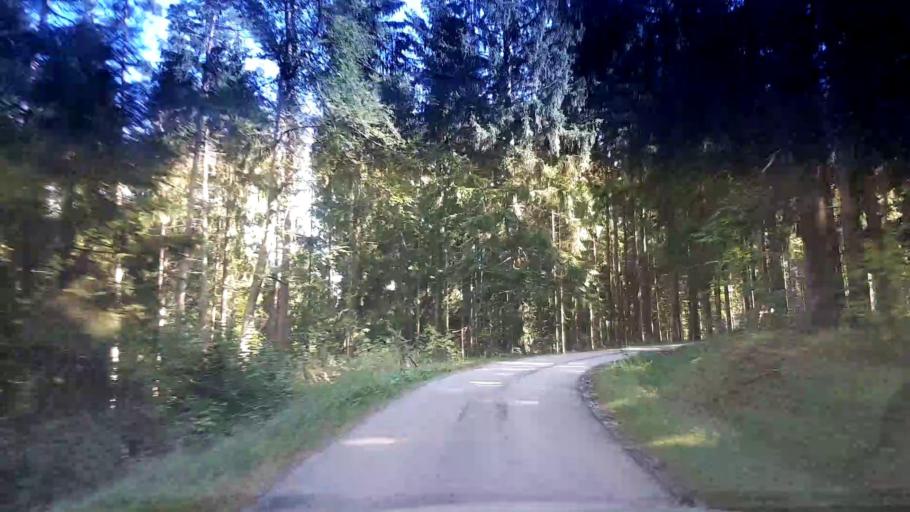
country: DE
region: Bavaria
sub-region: Upper Franconia
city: Poxdorf
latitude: 49.8835
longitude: 11.0872
